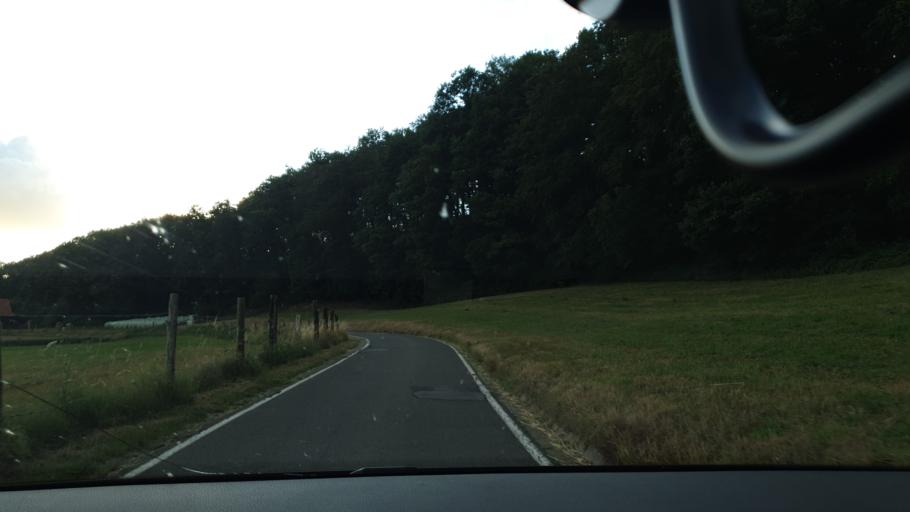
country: DE
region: Rheinland-Pfalz
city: Otterberg
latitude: 49.5078
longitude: 7.7506
